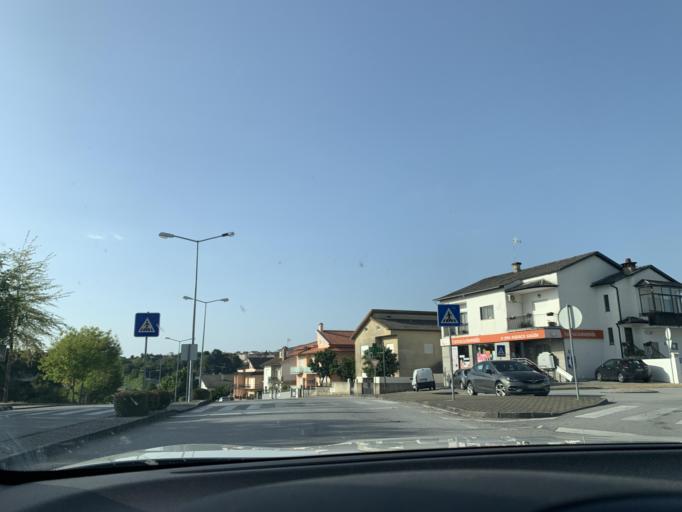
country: PT
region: Viseu
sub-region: Mangualde
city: Mangualde
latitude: 40.5953
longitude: -7.7573
